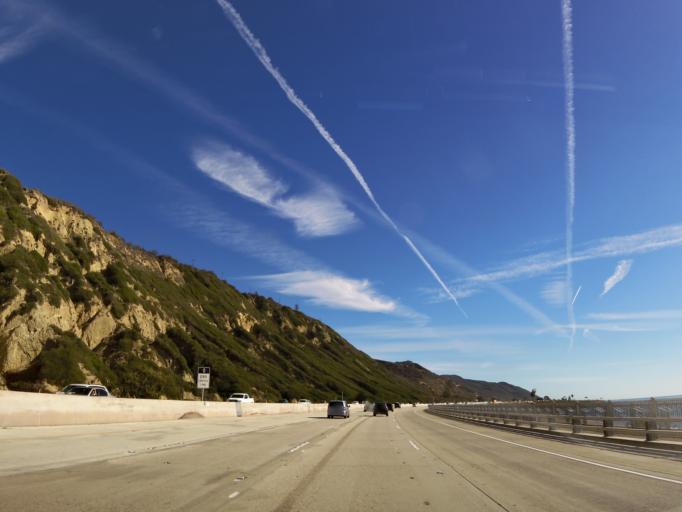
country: US
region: California
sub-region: Santa Barbara County
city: Carpinteria
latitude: 34.3554
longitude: -119.4316
